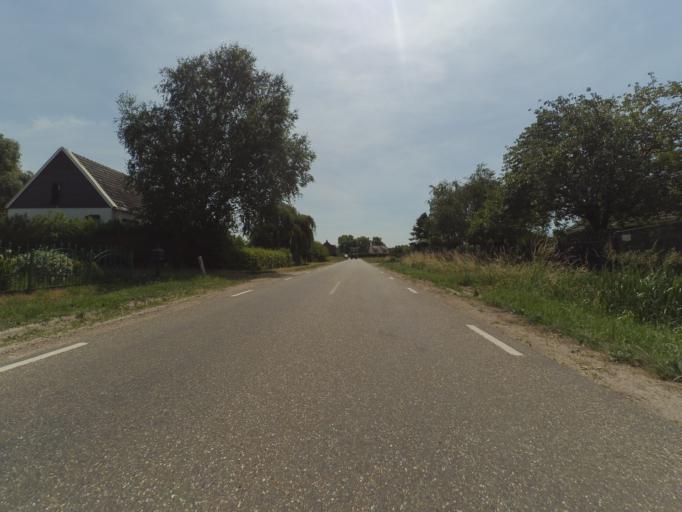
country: NL
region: North Brabant
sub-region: Gemeente Steenbergen
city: Kruisland
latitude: 51.5423
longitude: 4.3742
